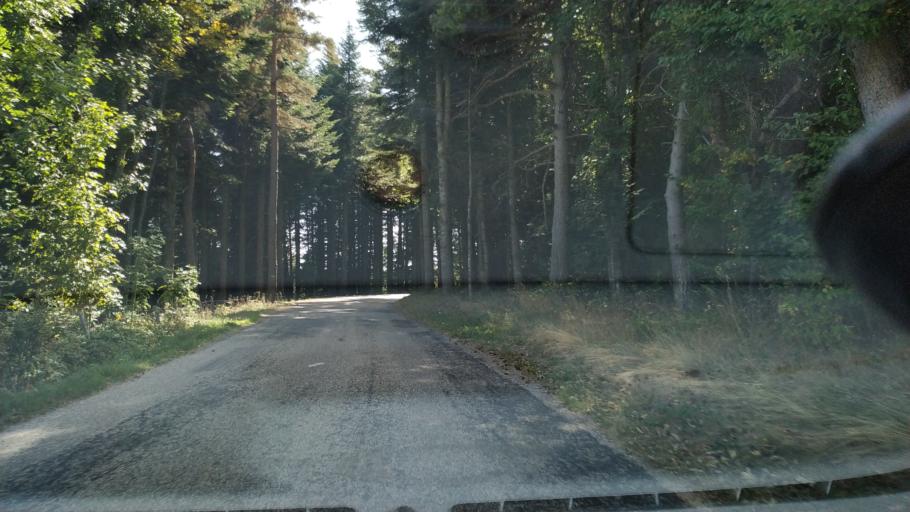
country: FR
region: Rhone-Alpes
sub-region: Departement de l'Ardeche
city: Saint-Agreve
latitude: 45.0312
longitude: 4.4236
